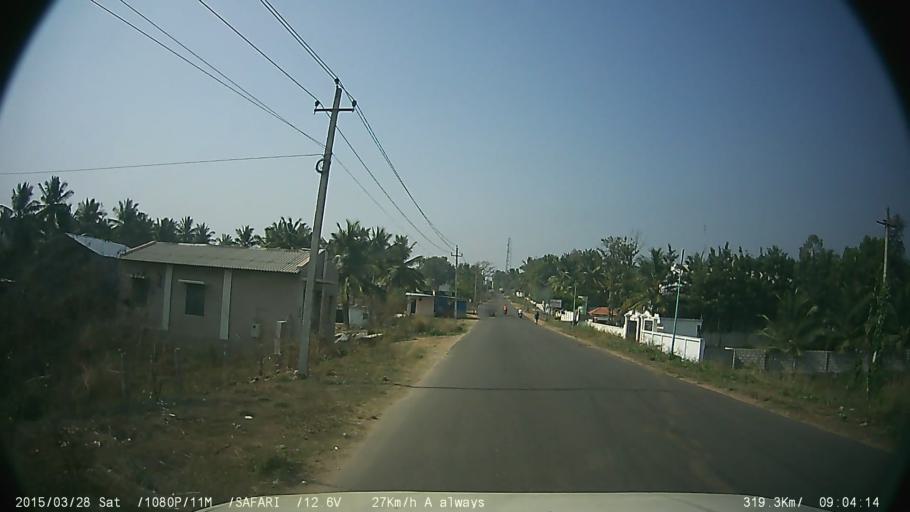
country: IN
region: Karnataka
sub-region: Mysore
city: Mysore
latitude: 12.3542
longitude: 76.5973
